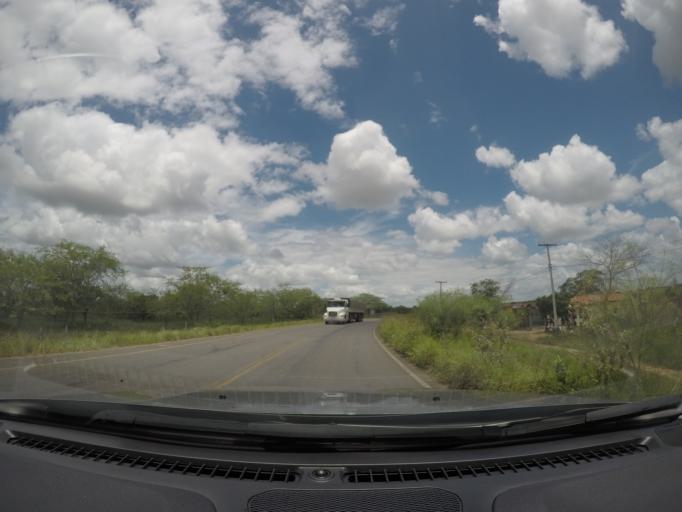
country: BR
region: Bahia
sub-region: Itaberaba
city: Itaberaba
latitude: -12.3572
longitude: -40.0382
